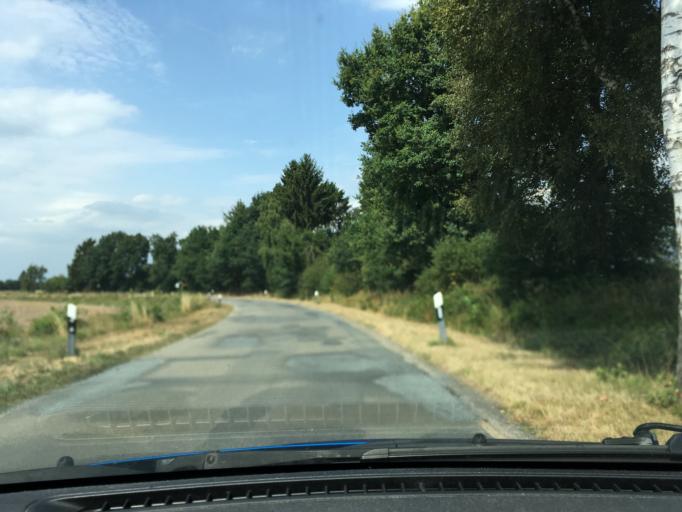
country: DE
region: Lower Saxony
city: Natendorf
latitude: 53.1228
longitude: 10.4310
